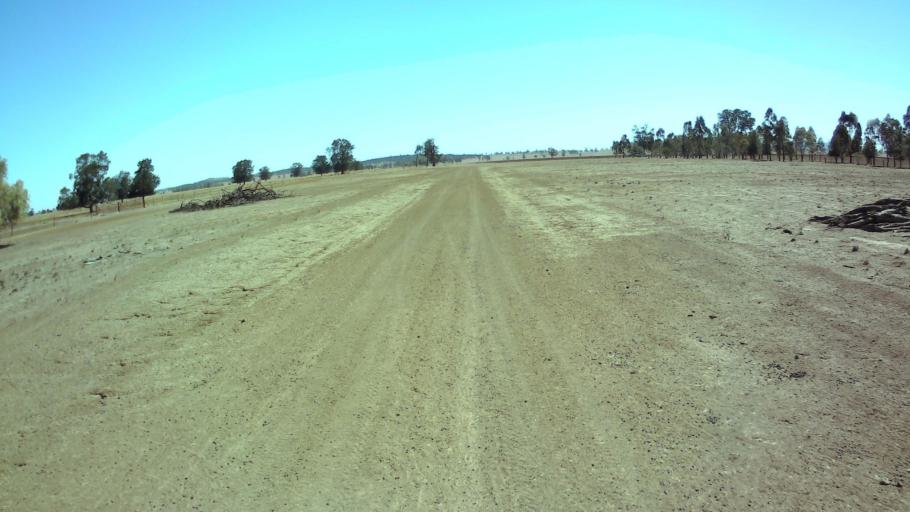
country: AU
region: New South Wales
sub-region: Forbes
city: Forbes
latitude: -33.7149
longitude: 147.6668
